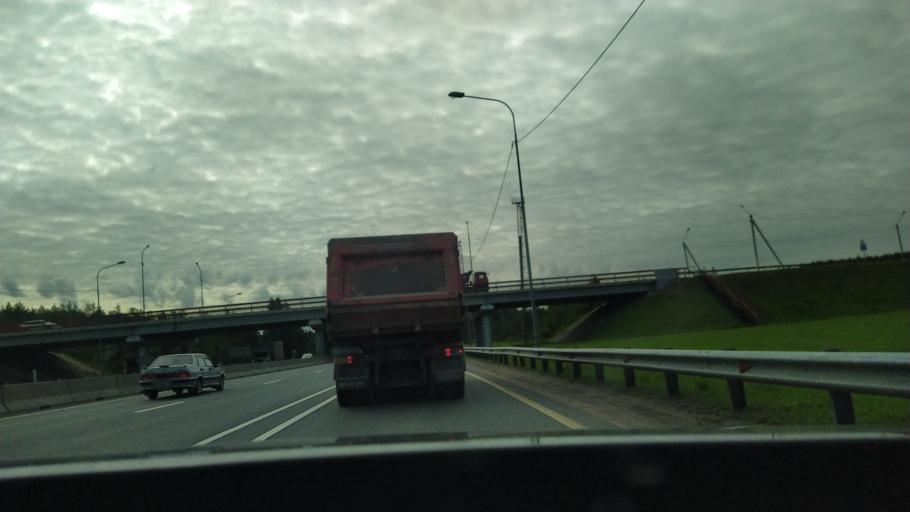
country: RU
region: Leningrad
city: Ul'yanovka
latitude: 59.6062
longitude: 30.7577
